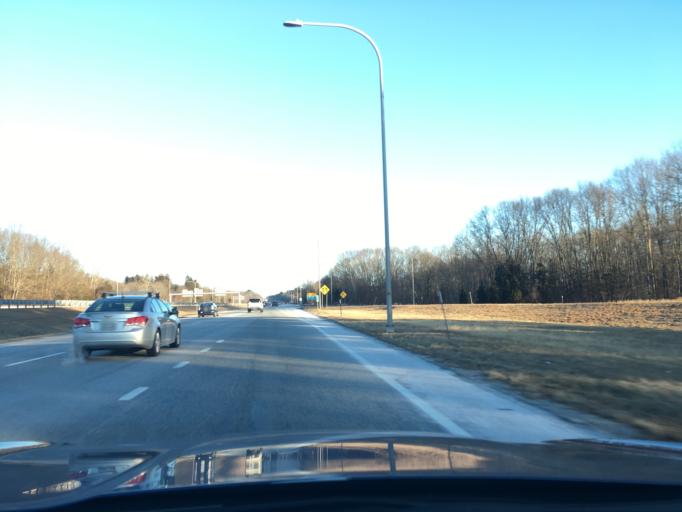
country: US
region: Rhode Island
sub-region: Kent County
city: East Greenwich
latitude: 41.6306
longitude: -71.4868
